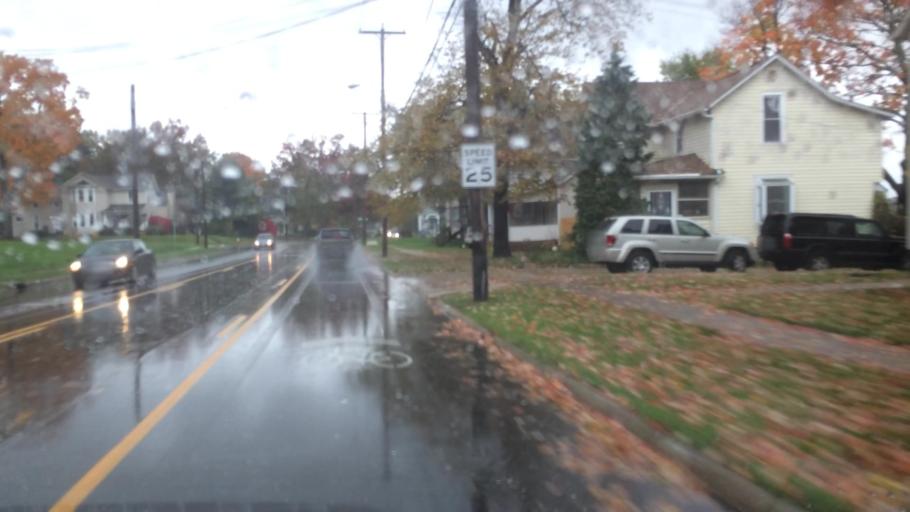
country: US
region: Ohio
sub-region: Summit County
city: Cuyahoga Falls
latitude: 41.1398
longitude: -81.4825
